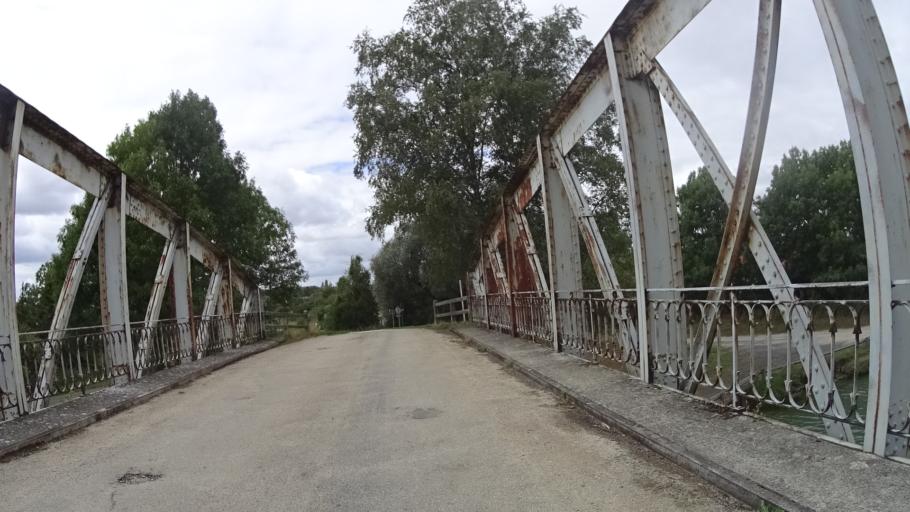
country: FR
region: Picardie
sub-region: Departement de l'Aisne
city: Viry-Noureuil
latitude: 49.6174
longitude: 3.2428
